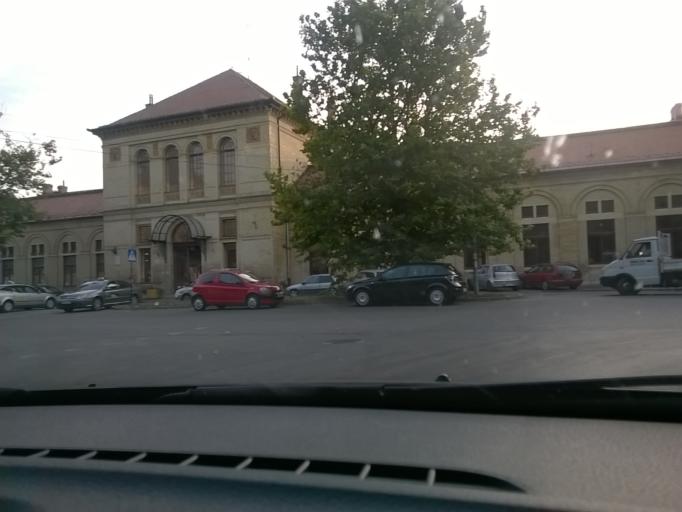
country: RS
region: Autonomna Pokrajina Vojvodina
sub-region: Juznobanatski Okrug
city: Vrsac
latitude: 45.1061
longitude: 21.2842
